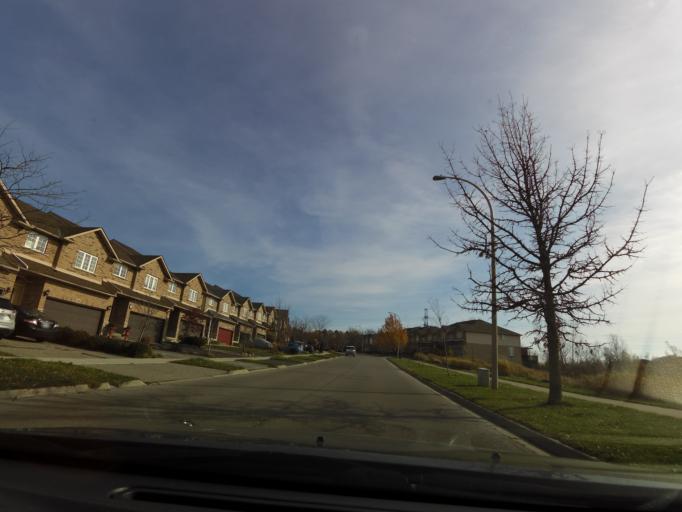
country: CA
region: Ontario
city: Ancaster
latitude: 43.2266
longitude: -79.9391
